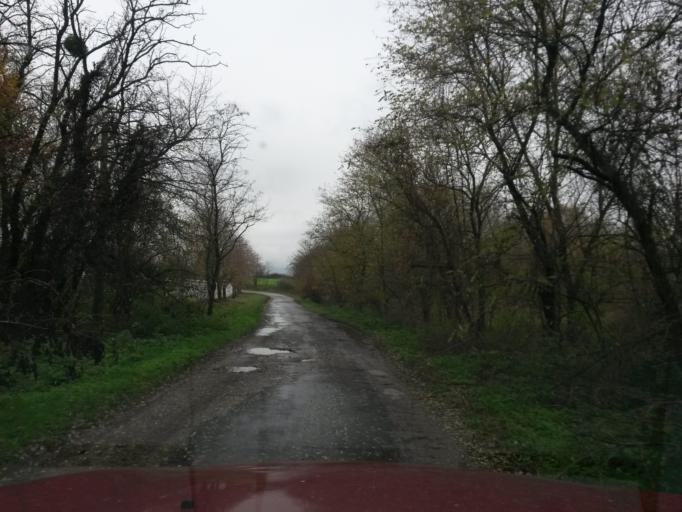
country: SK
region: Kosicky
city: Cierna nad Tisou
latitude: 48.5566
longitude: 21.9504
